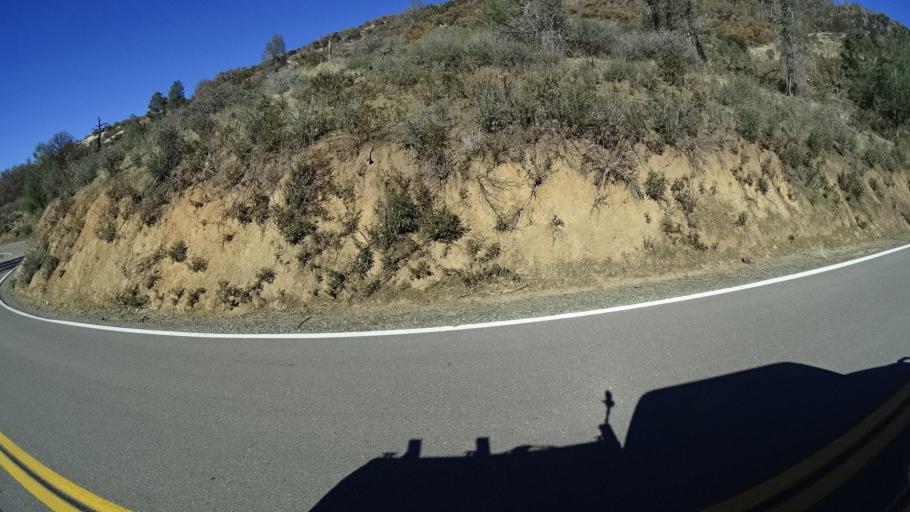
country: US
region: California
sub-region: Kern County
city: Alta Sierra
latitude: 35.7462
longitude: -118.5941
